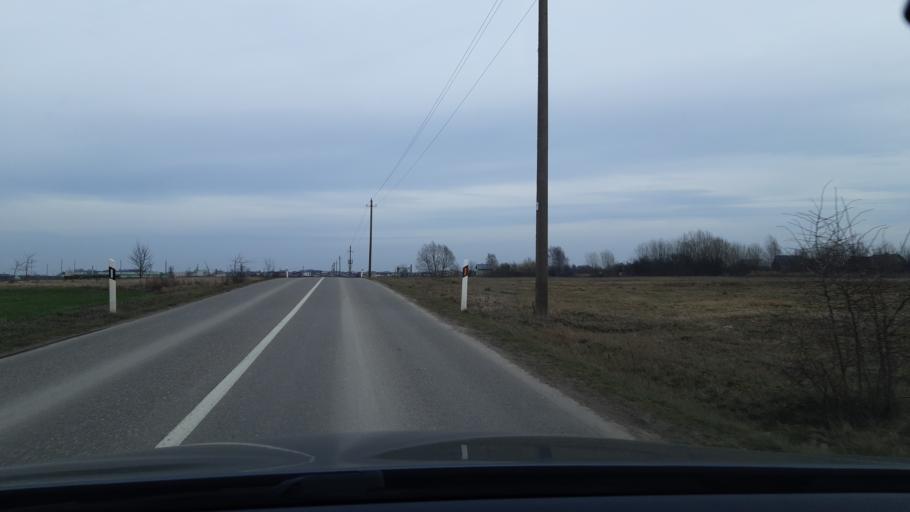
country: LT
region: Kauno apskritis
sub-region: Kaunas
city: Sargenai
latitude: 54.9485
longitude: 23.8352
